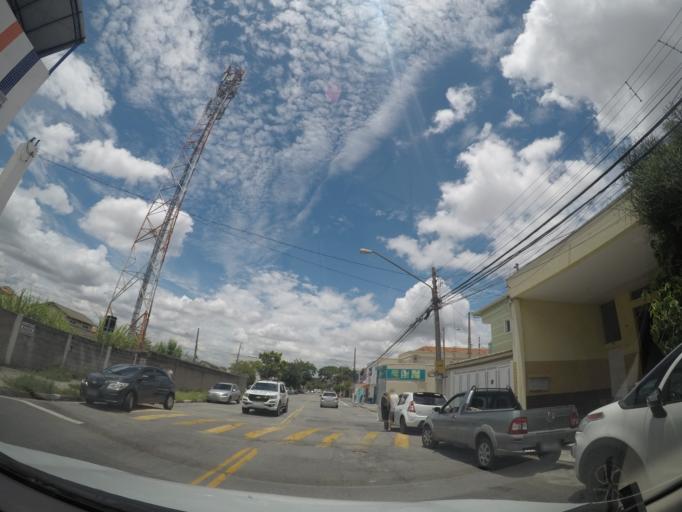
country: BR
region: Sao Paulo
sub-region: Guarulhos
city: Guarulhos
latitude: -23.4469
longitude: -46.5308
